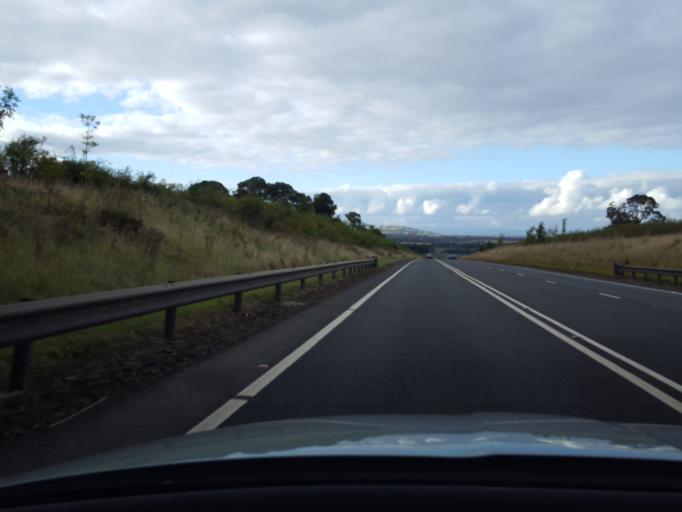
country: GB
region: Scotland
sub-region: Midlothian
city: Dalkeith
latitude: 55.9026
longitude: -3.0275
